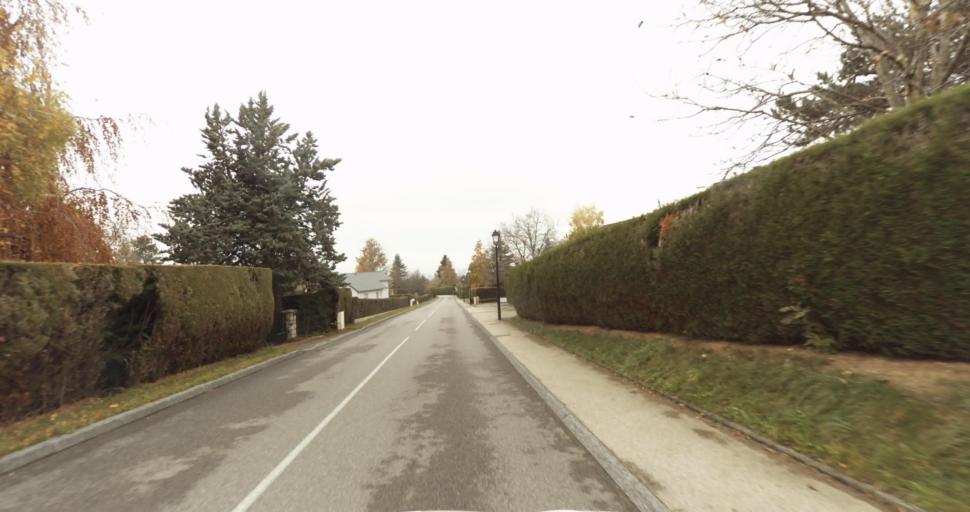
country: FR
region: Rhone-Alpes
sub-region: Departement de la Haute-Savoie
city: Seynod
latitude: 45.8467
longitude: 6.0846
